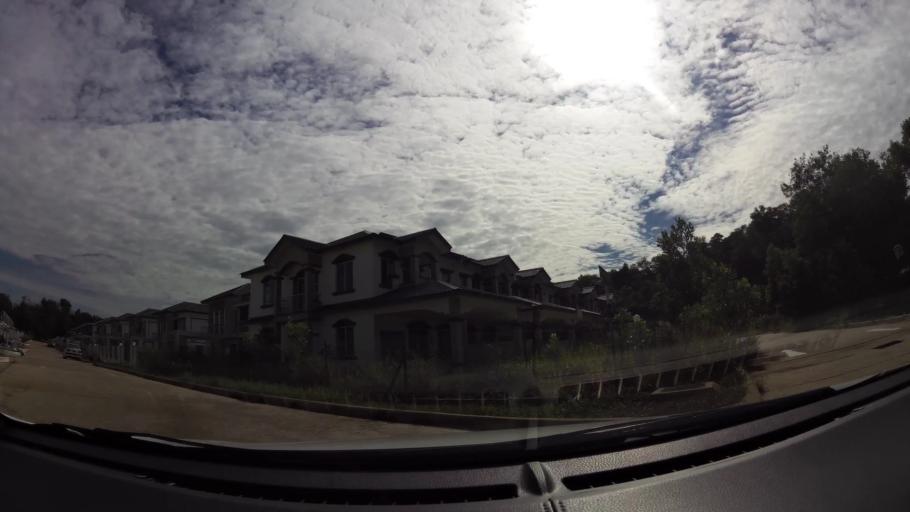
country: BN
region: Brunei and Muara
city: Bandar Seri Begawan
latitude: 4.9237
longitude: 114.8984
